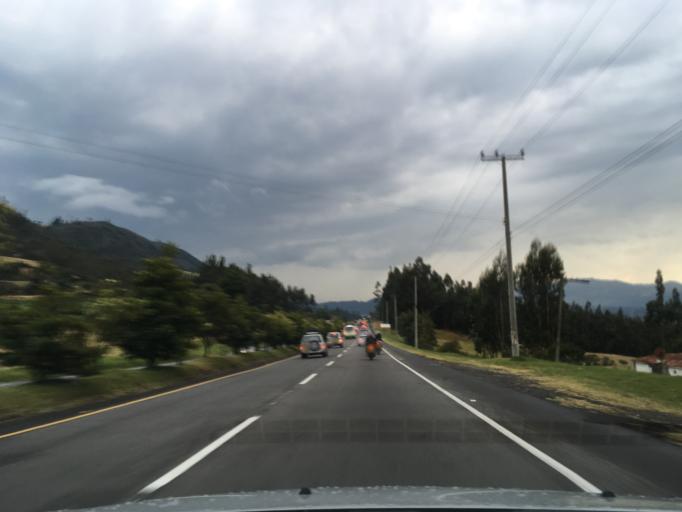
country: CO
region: Cundinamarca
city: Sesquile
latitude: 5.0679
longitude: -73.7609
